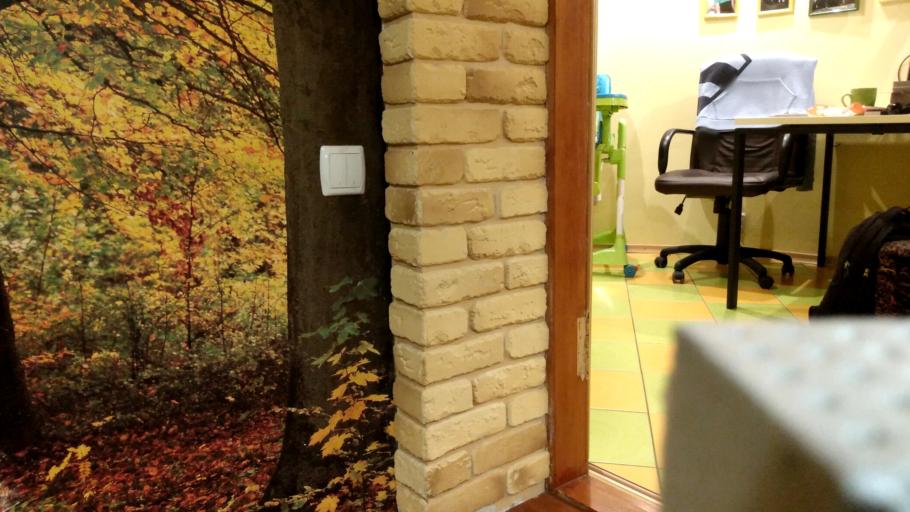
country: RU
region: Republic of Karelia
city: Pudozh
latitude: 61.7638
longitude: 37.6849
